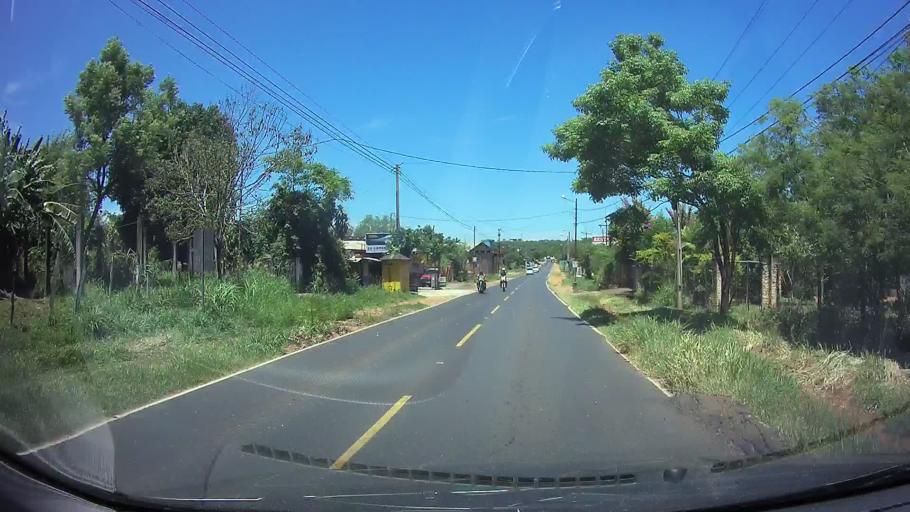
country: PY
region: Central
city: Limpio
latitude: -25.2479
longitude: -57.4855
